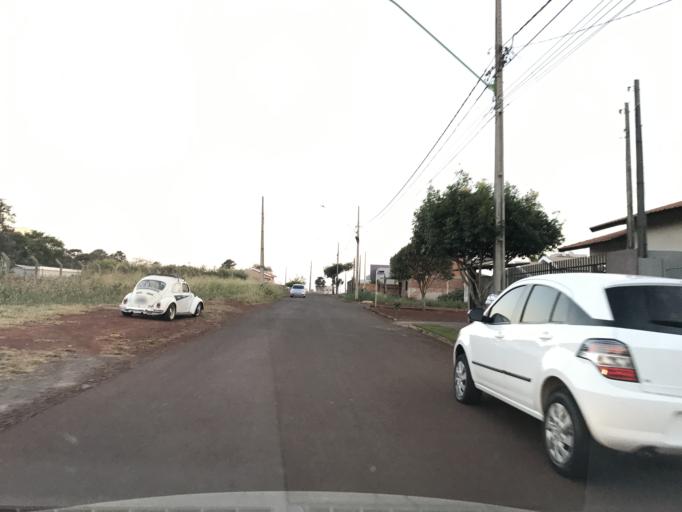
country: BR
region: Parana
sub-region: Palotina
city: Palotina
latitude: -24.3046
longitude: -53.8369
